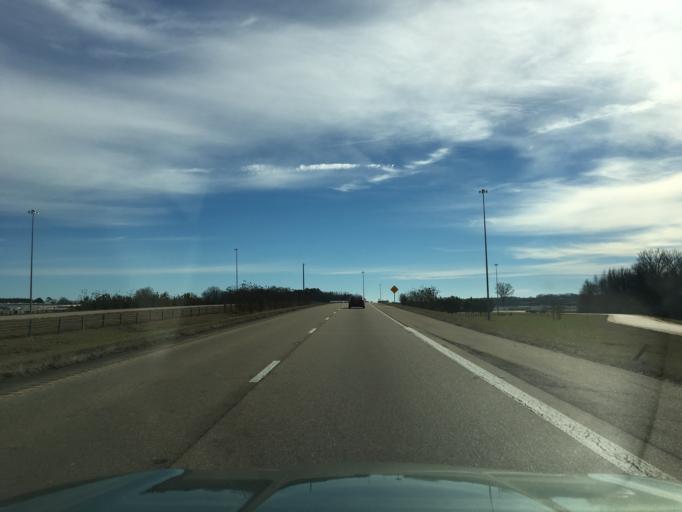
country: US
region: Mississippi
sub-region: Lee County
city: Saltillo
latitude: 34.3564
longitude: -88.8437
